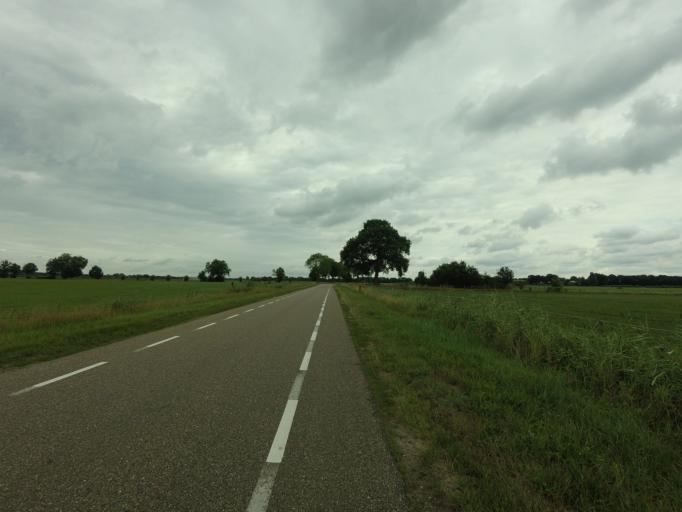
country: NL
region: Gelderland
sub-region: Gemeente Lochem
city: Laren
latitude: 52.2872
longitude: 6.3498
